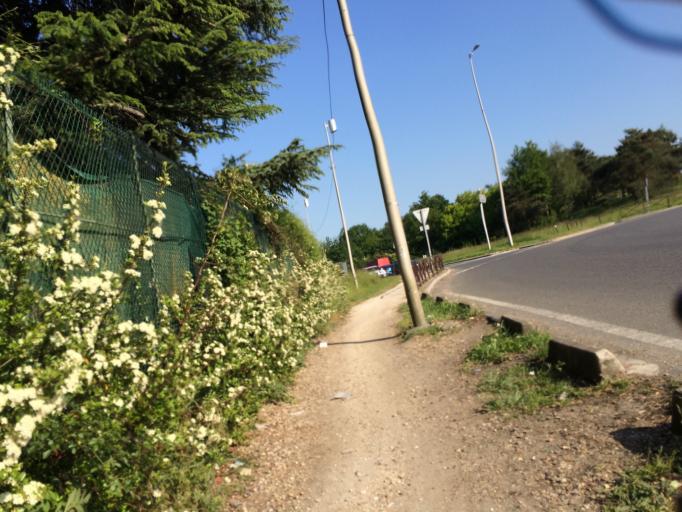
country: FR
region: Ile-de-France
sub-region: Departement de l'Essonne
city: Bondoufle
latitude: 48.6260
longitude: 2.3887
